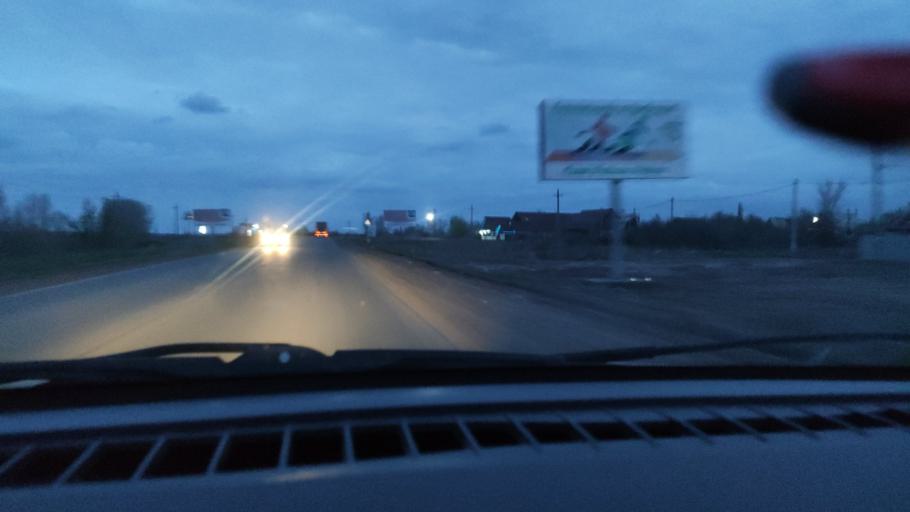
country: RU
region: Orenburg
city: Tatarskaya Kargala
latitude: 51.9024
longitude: 55.1684
